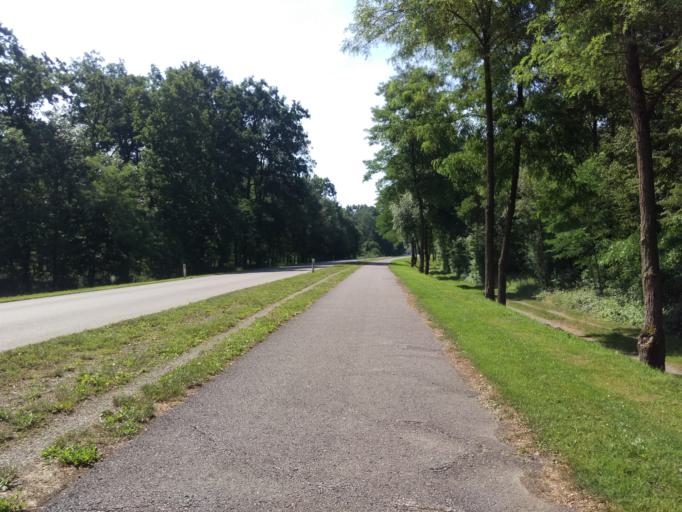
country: AT
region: Styria
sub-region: Politischer Bezirk Graz-Umgebung
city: Feldkirchen bei Graz
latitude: 47.0043
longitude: 15.4690
